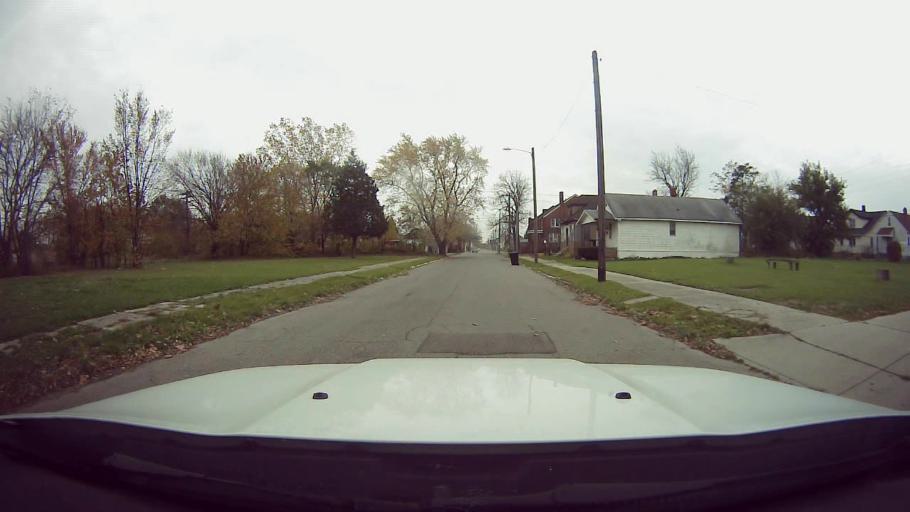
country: US
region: Michigan
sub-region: Wayne County
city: Hamtramck
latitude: 42.4061
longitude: -83.0673
